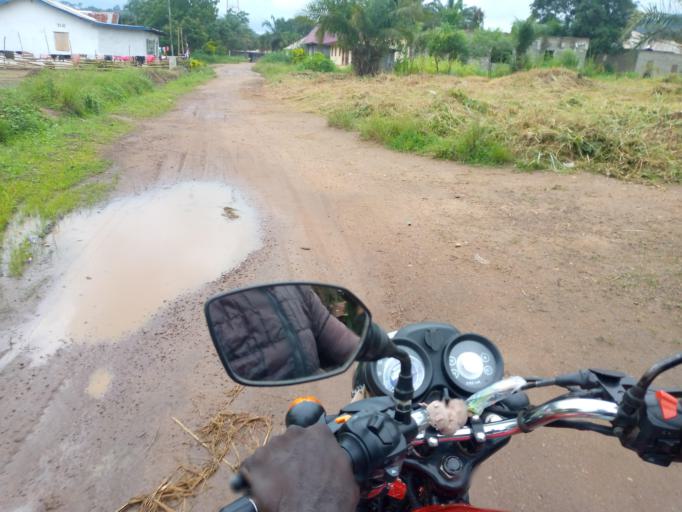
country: SL
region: Eastern Province
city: Kenema
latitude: 7.8470
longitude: -11.2036
